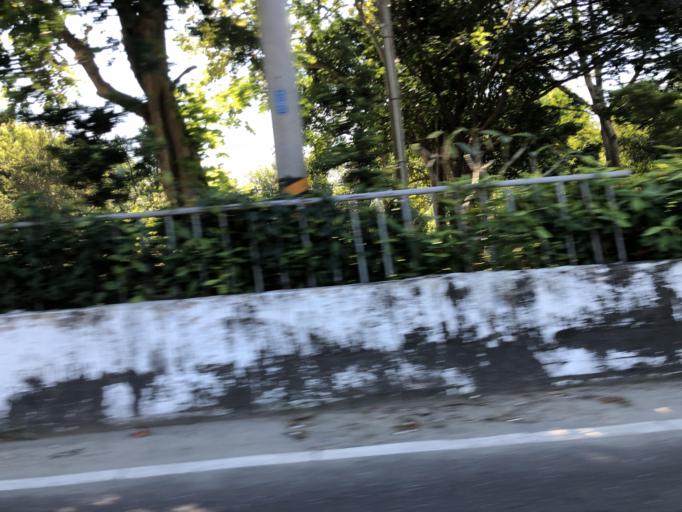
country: TW
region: Taiwan
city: Yujing
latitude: 23.0566
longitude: 120.3989
